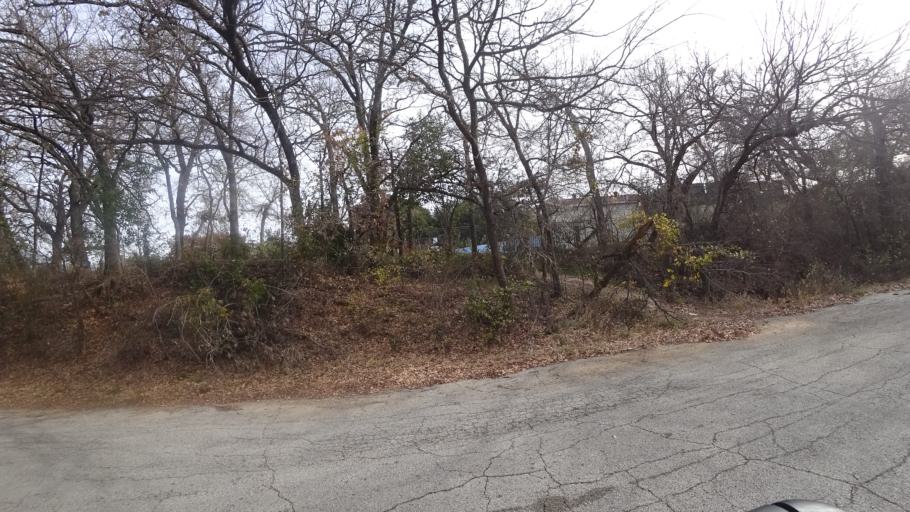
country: US
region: Texas
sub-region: Denton County
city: Highland Village
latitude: 33.0814
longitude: -97.0185
